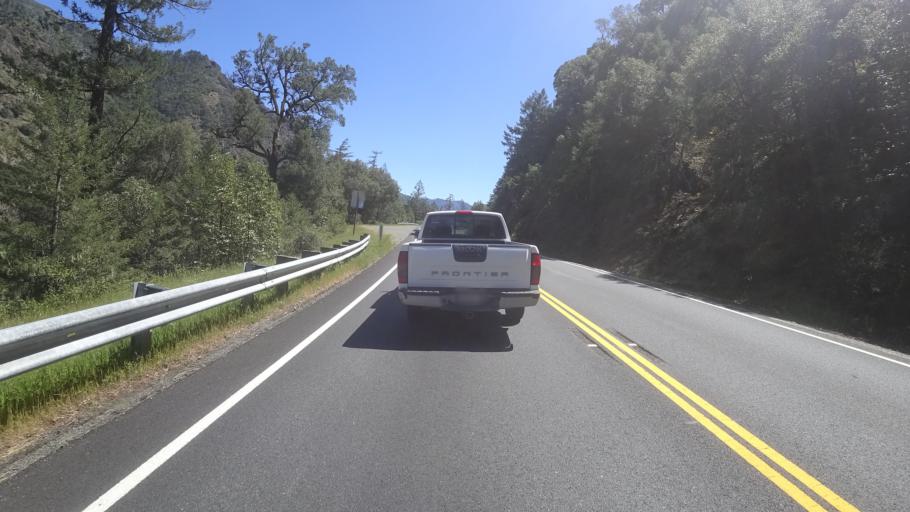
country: US
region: California
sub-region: Humboldt County
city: Willow Creek
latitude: 40.8182
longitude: -123.4797
